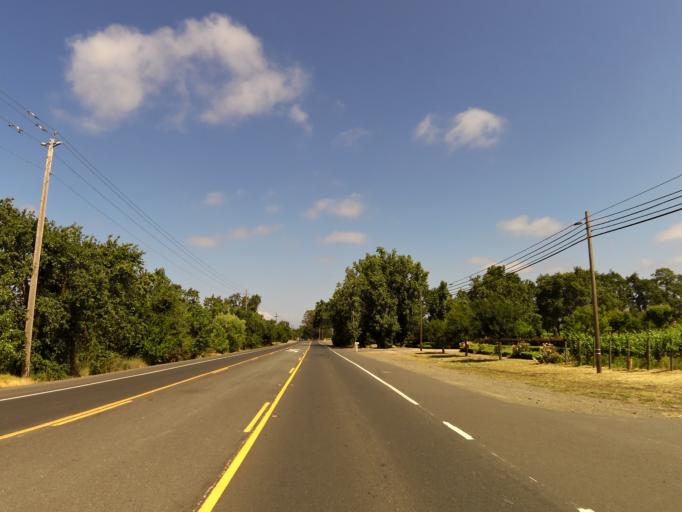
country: US
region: California
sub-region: Napa County
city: Yountville
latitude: 38.4253
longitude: -122.3925
